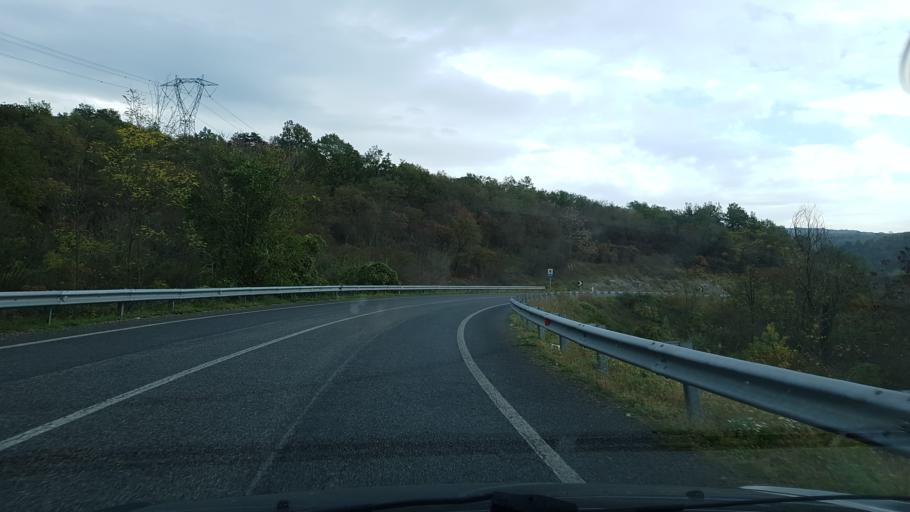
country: IT
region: Friuli Venezia Giulia
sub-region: Provincia di Gorizia
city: Doberdo del Lago
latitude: 45.8684
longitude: 13.5606
